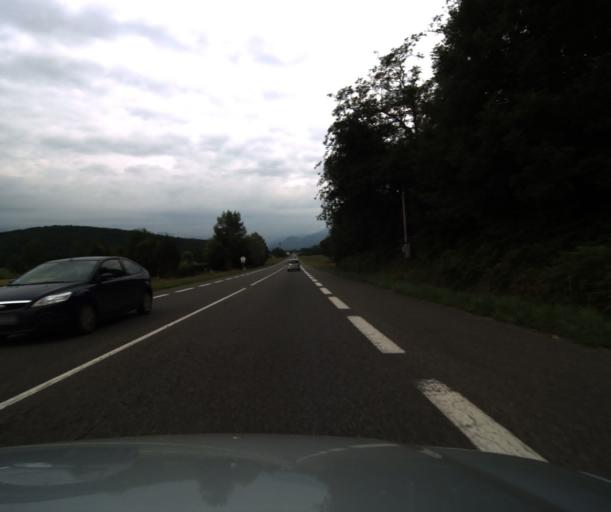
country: FR
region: Midi-Pyrenees
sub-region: Departement des Hautes-Pyrenees
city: Ossun
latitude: 43.1553
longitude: -0.0206
